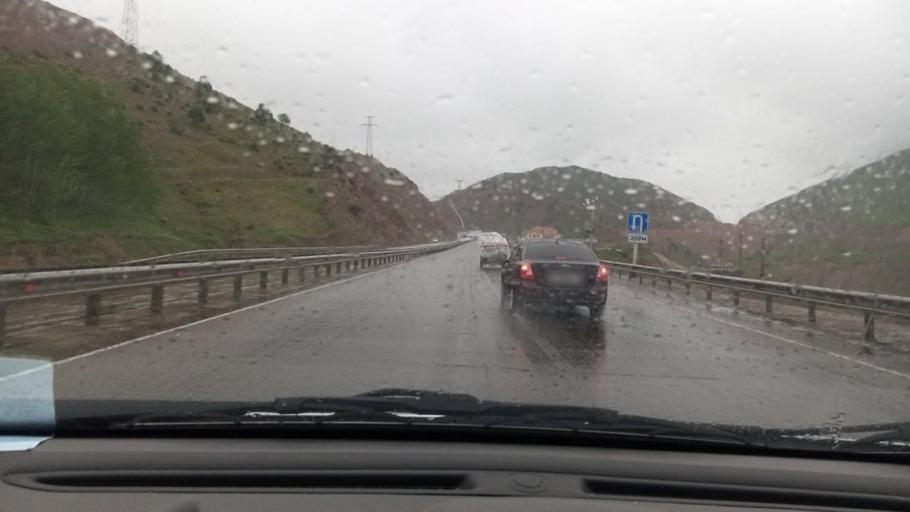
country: UZ
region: Toshkent
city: Angren
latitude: 41.0850
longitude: 70.5389
